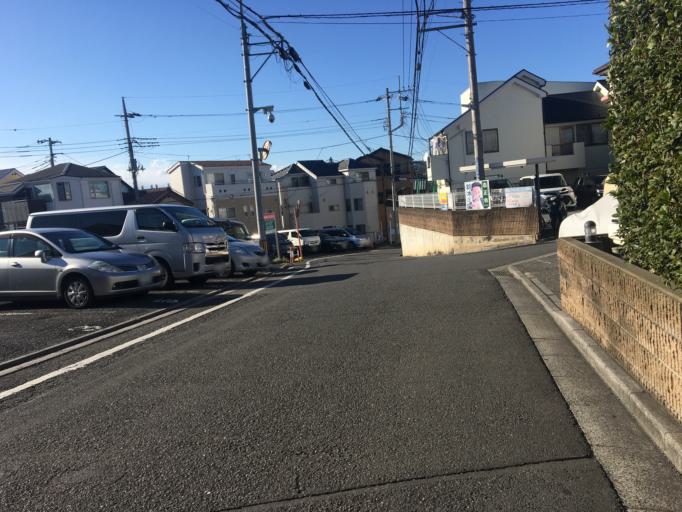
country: JP
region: Saitama
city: Shiki
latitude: 35.8235
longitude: 139.5626
